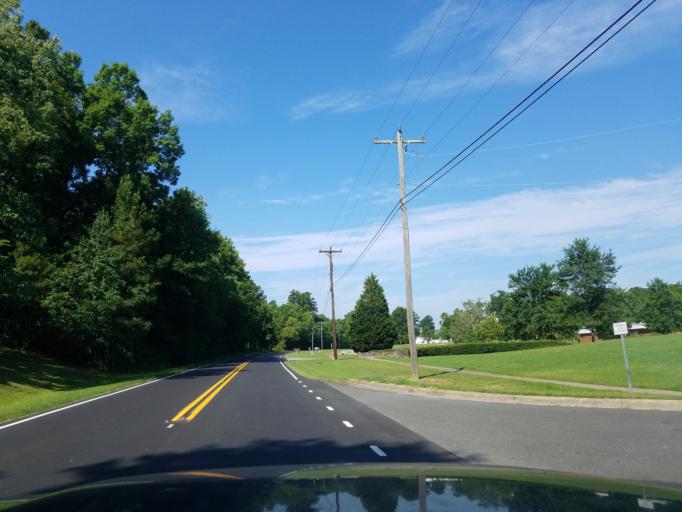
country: US
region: North Carolina
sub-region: Durham County
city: Gorman
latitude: 36.0280
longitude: -78.8359
